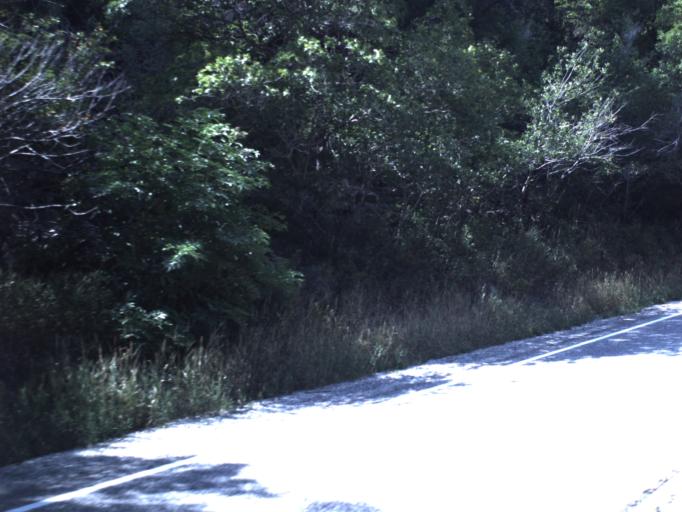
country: US
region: Utah
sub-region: Cache County
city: North Logan
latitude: 41.8123
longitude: -111.6249
